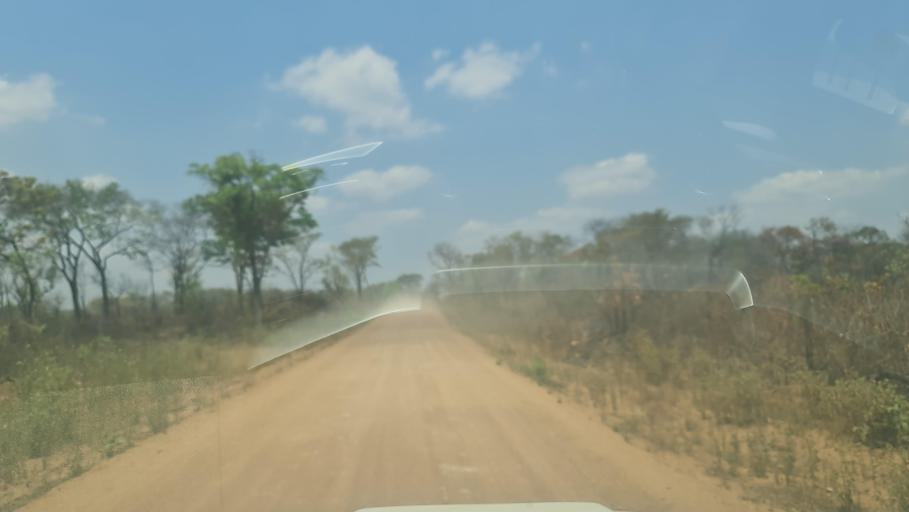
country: MW
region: Southern Region
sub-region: Nsanje District
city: Nsanje
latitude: -17.5569
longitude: 35.8968
